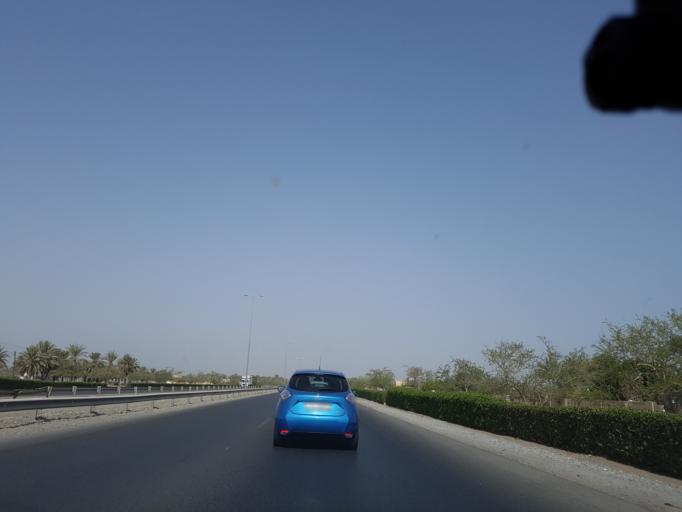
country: OM
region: Al Batinah
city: Barka'
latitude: 23.7369
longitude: 57.6597
